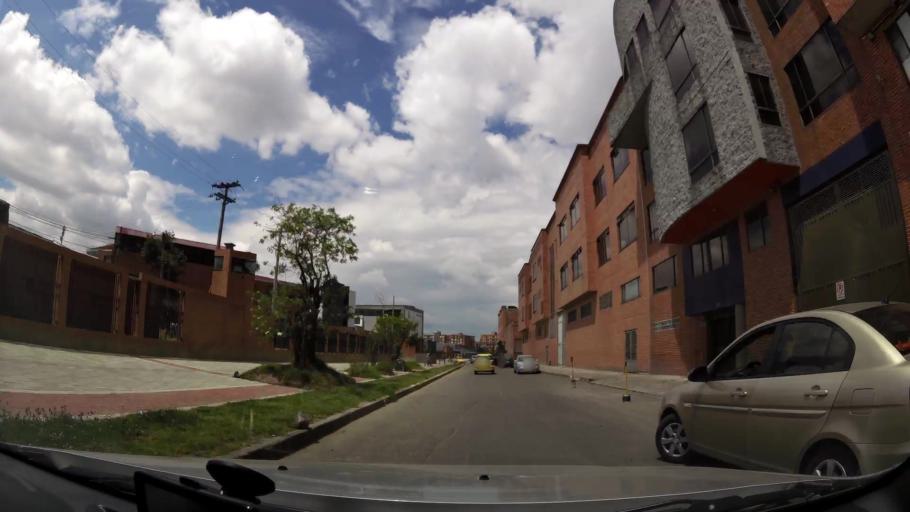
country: CO
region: Bogota D.C.
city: Bogota
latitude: 4.6301
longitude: -74.1009
